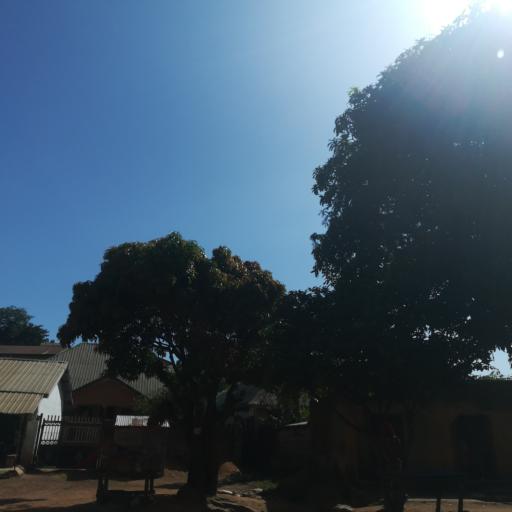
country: NG
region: Plateau
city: Jos
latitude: 9.9415
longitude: 8.9073
